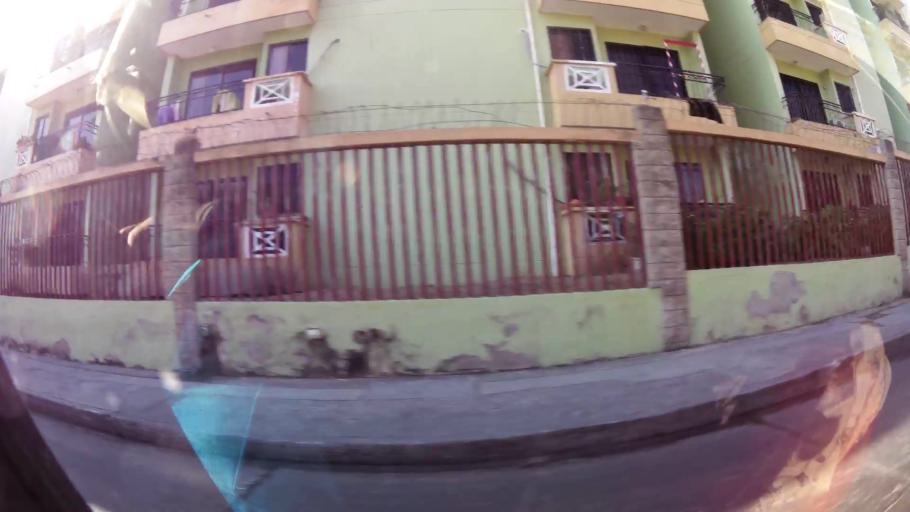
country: CO
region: Atlantico
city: Barranquilla
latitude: 10.9854
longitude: -74.7893
